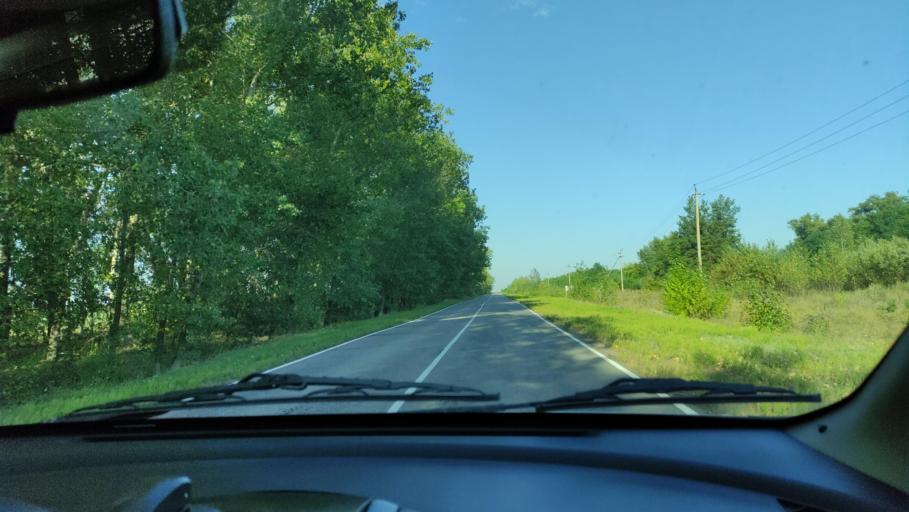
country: RU
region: Voronezj
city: Verkhniy Mamon
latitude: 50.1189
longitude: 40.2975
